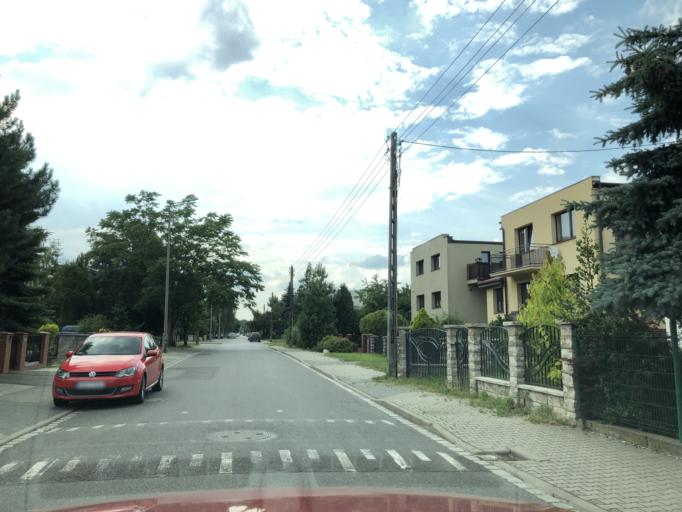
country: PL
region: Lower Silesian Voivodeship
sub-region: Powiat wroclawski
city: Smolec
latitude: 51.1561
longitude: 16.9051
